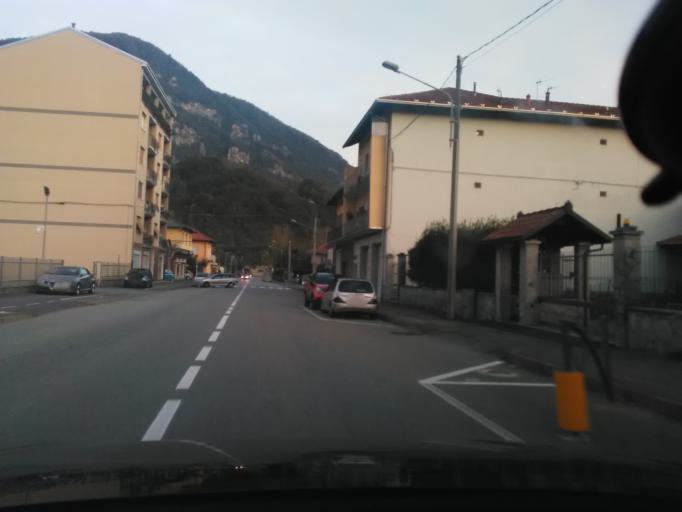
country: IT
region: Piedmont
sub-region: Provincia di Vercelli
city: Borgosesia
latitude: 45.7100
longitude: 8.2956
